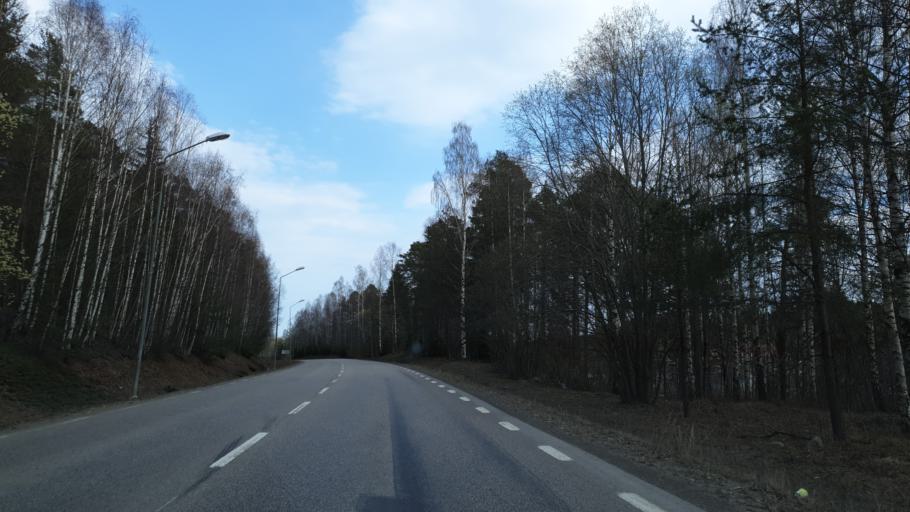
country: SE
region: Gaevleborg
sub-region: Hudiksvalls Kommun
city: Iggesund
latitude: 61.6419
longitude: 17.0663
